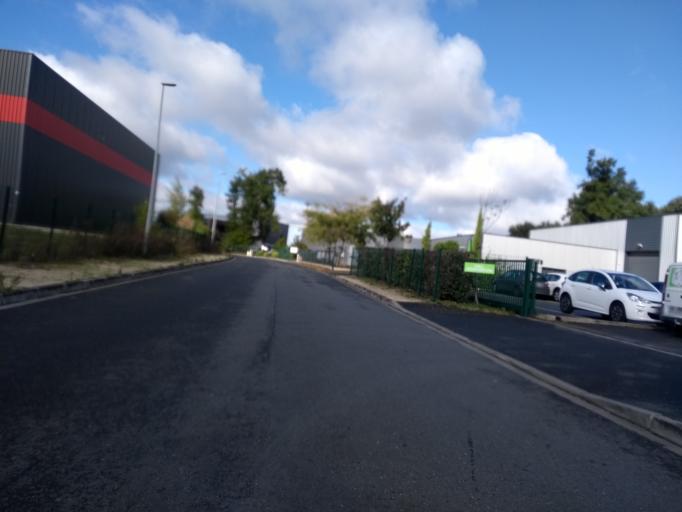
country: FR
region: Aquitaine
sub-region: Departement de la Gironde
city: Canejan
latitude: 44.7725
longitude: -0.6484
